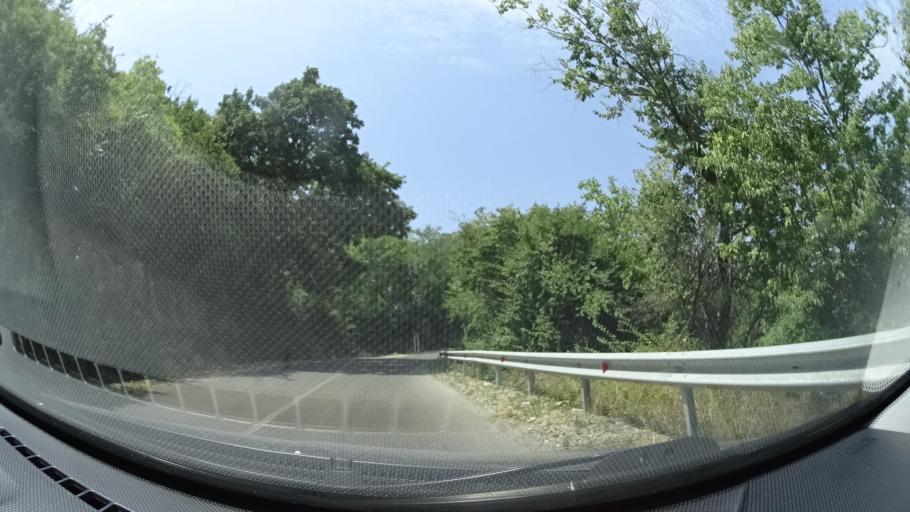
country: GE
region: Kakheti
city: Sighnaghi
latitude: 41.6219
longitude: 45.9300
